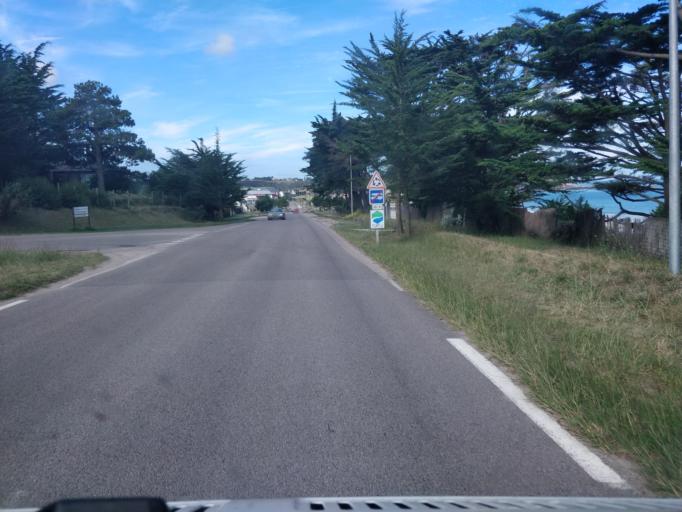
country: FR
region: Brittany
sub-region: Departement des Cotes-d'Armor
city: Plurien
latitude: 48.6414
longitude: -2.3974
